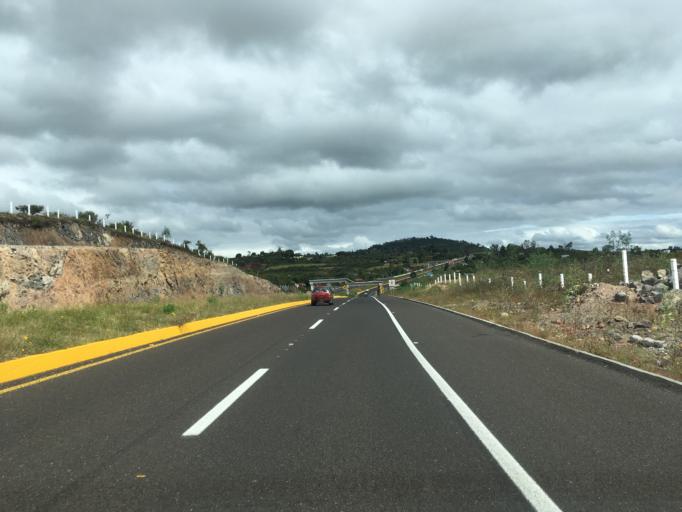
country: MX
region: Hidalgo
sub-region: Atotonilco el Grande
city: Santa Maria Amajac
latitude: 20.3895
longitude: -98.7234
